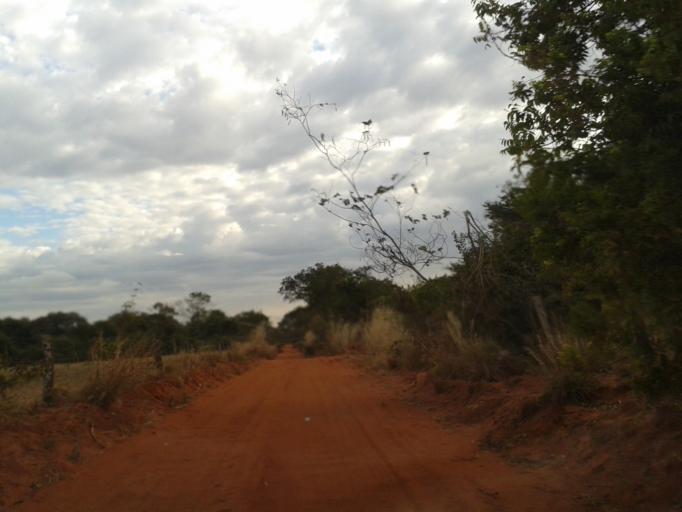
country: BR
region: Minas Gerais
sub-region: Santa Vitoria
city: Santa Vitoria
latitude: -18.7699
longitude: -50.1876
